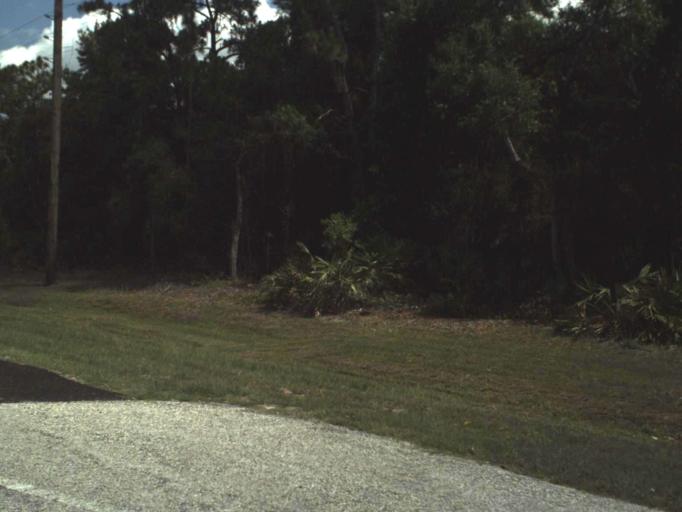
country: US
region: Florida
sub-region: Lake County
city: Mount Dora
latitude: 28.8171
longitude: -81.6305
